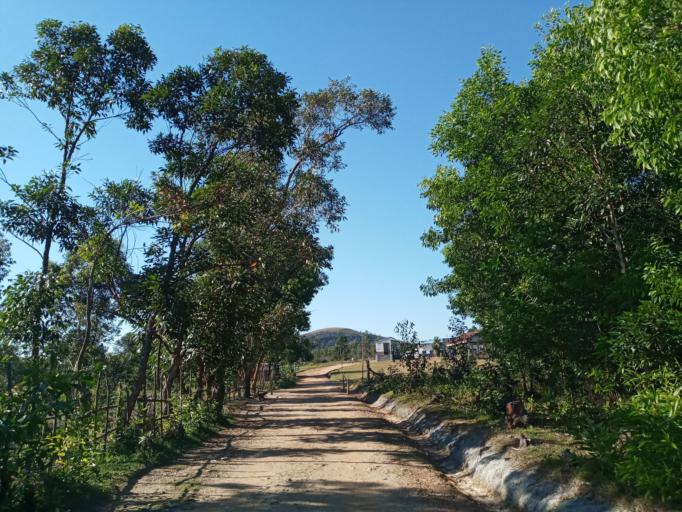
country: MG
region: Anosy
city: Fort Dauphin
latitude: -24.9099
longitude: 47.0324
